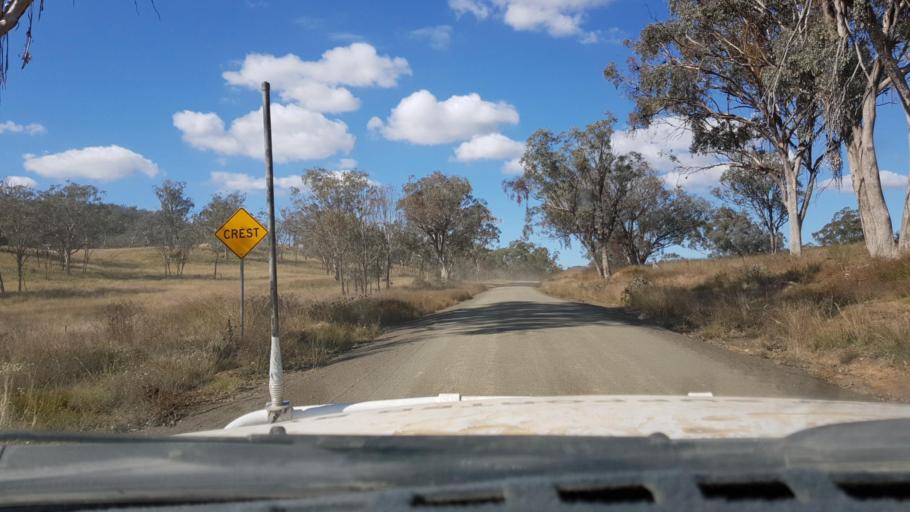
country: AU
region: New South Wales
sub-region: Tamworth Municipality
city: Manilla
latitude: -30.4760
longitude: 150.7590
